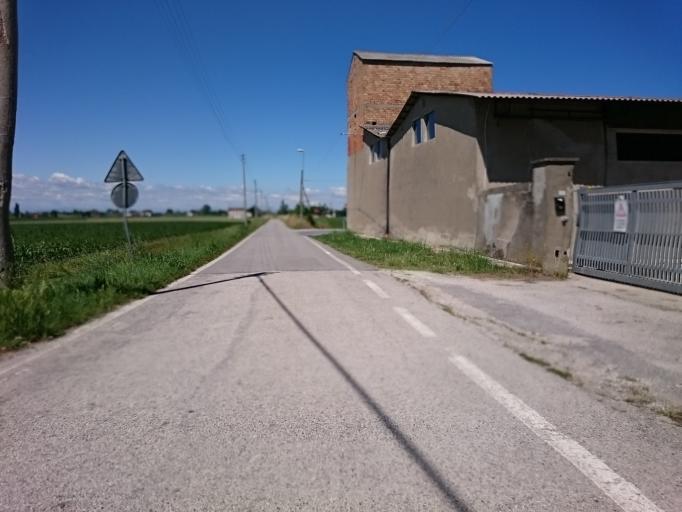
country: IT
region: Veneto
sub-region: Provincia di Padova
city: Codevigo
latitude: 45.2338
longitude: 12.1143
